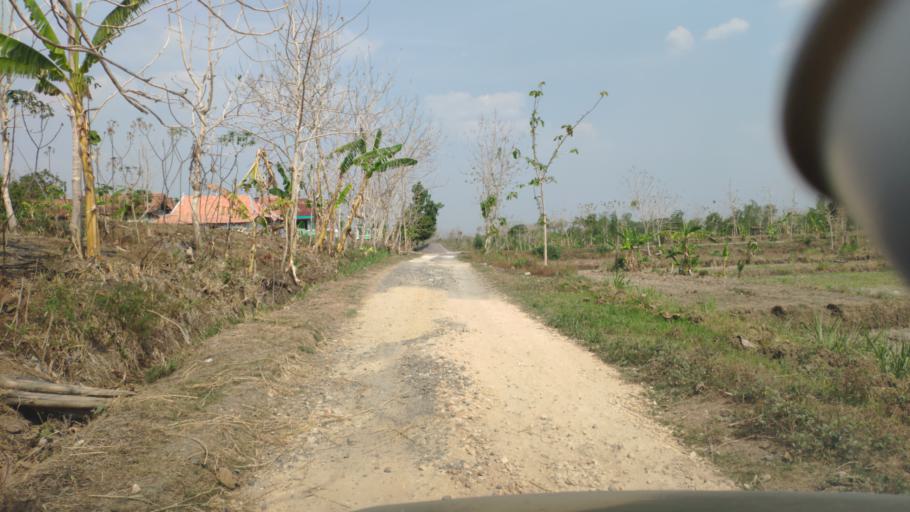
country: ID
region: Central Java
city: Jagong
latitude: -7.0870
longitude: 111.2249
